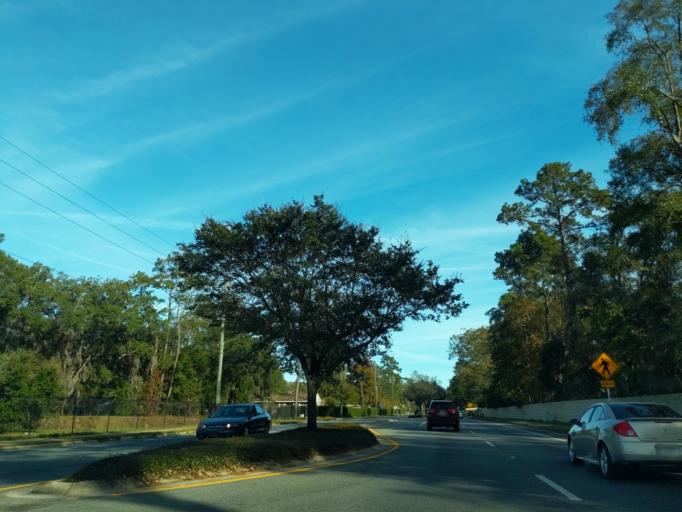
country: US
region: Florida
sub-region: Leon County
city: Tallahassee
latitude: 30.4126
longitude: -84.2724
